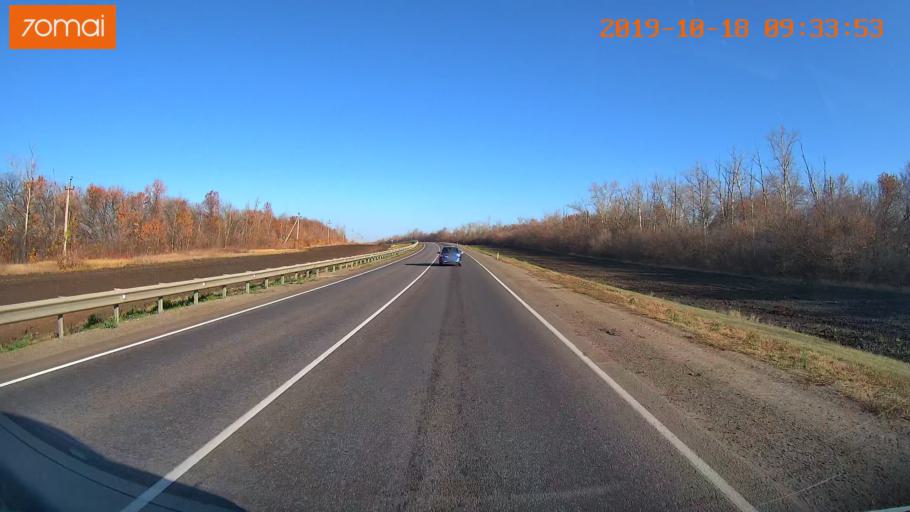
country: RU
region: Tula
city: Yefremov
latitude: 53.1729
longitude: 38.1525
